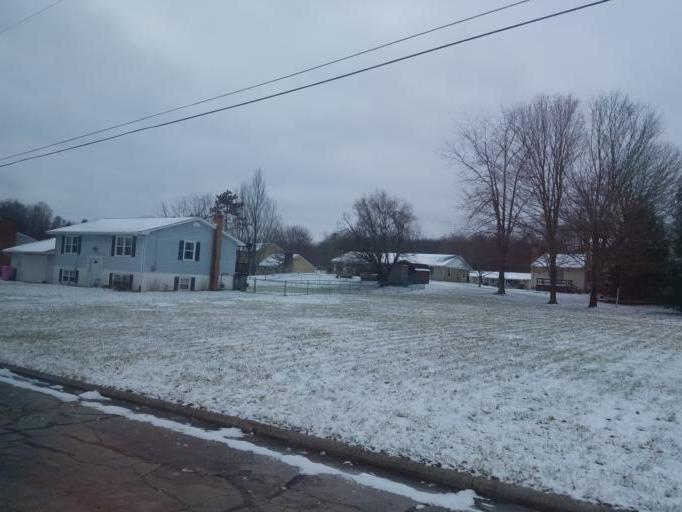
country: US
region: Ohio
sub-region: Richland County
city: Lexington
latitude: 40.6721
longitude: -82.5996
